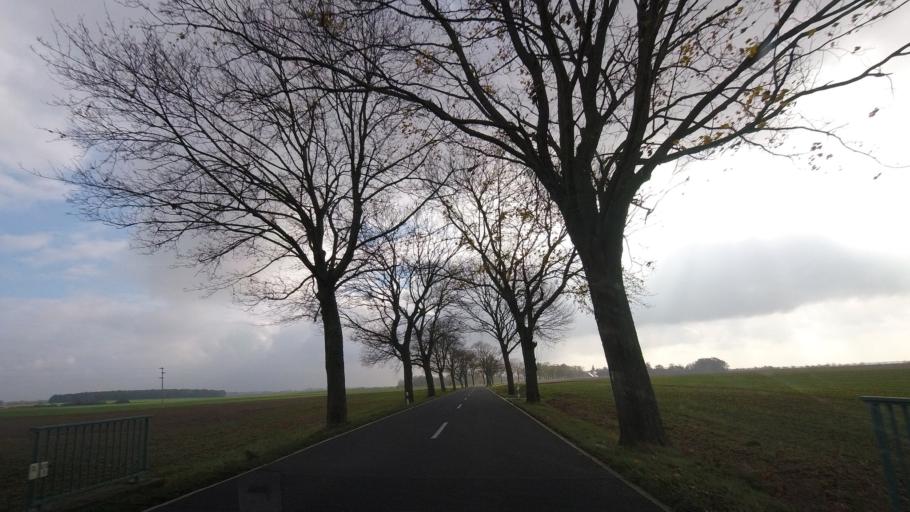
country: DE
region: Brandenburg
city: Niedergorsdorf
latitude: 51.9918
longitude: 12.9419
